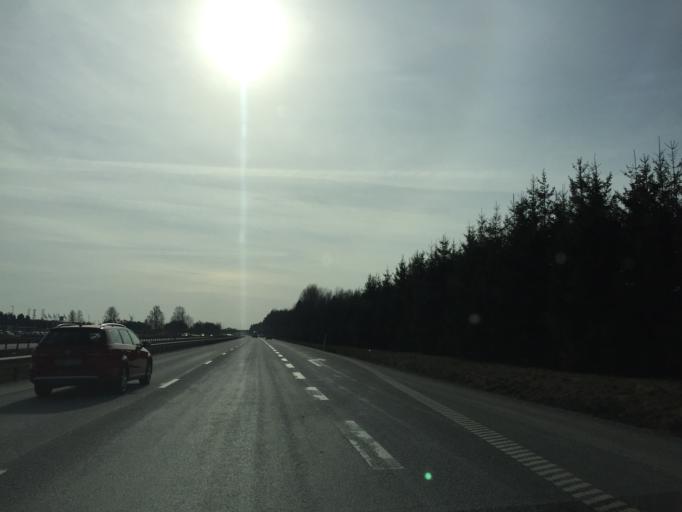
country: SE
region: OErebro
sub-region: Orebro Kommun
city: Orebro
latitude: 59.2210
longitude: 15.1359
